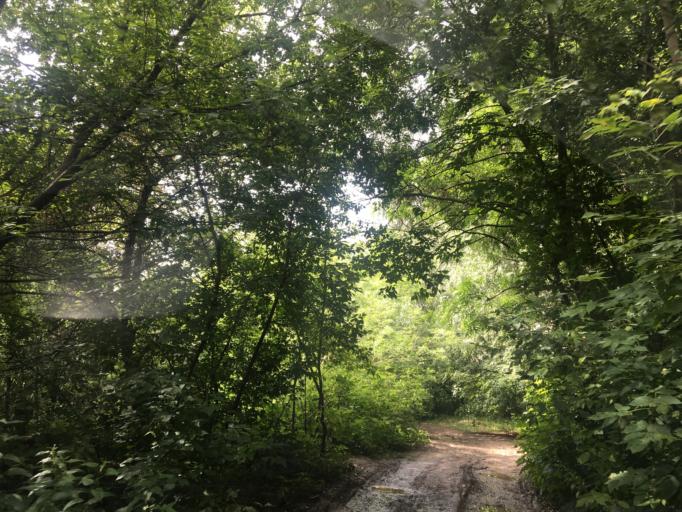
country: RU
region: Tula
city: Mendeleyevskiy
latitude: 54.1495
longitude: 37.5875
